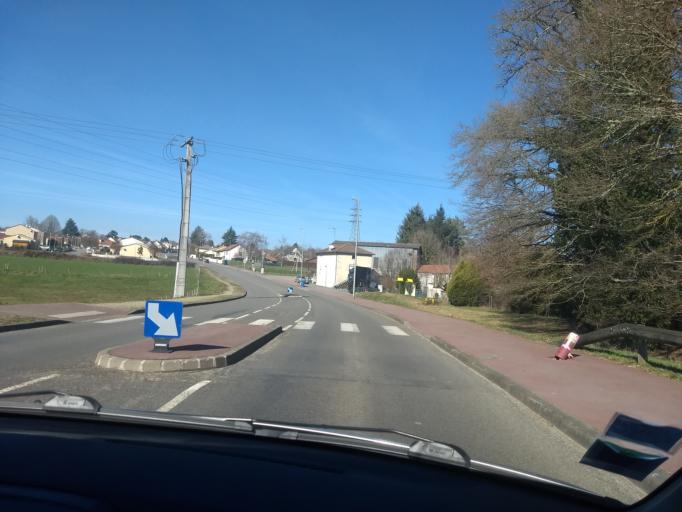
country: FR
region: Limousin
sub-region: Departement de la Haute-Vienne
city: Isle
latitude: 45.8222
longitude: 1.2083
